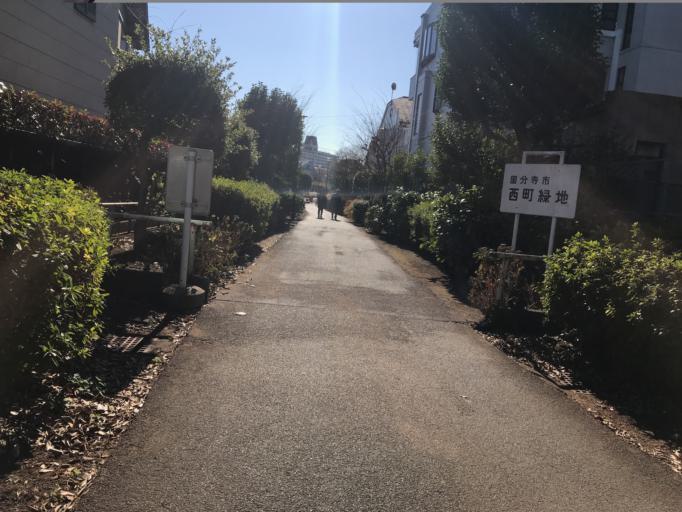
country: JP
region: Tokyo
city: Kokubunji
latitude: 35.7040
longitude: 139.4326
